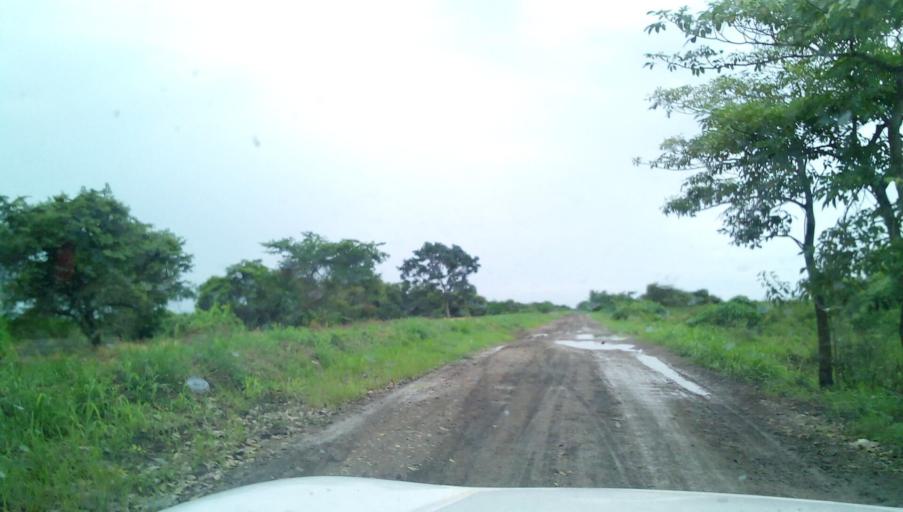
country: MX
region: Veracruz
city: Panuco
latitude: 21.8274
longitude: -98.1108
